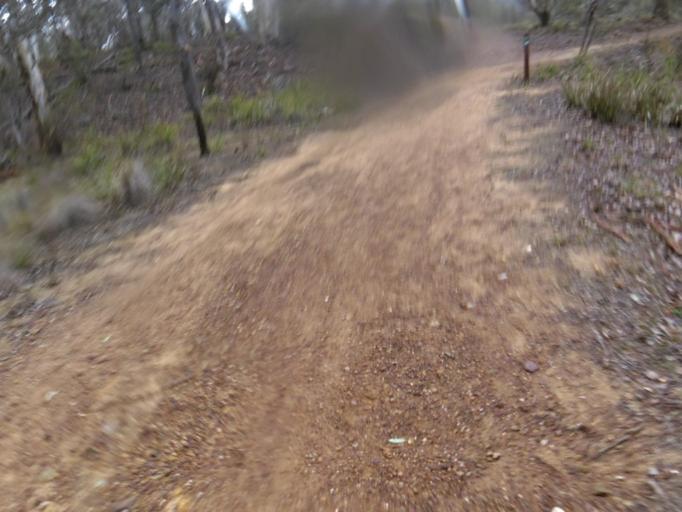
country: AU
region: Australian Capital Territory
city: Macquarie
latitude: -35.2677
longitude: 149.0882
